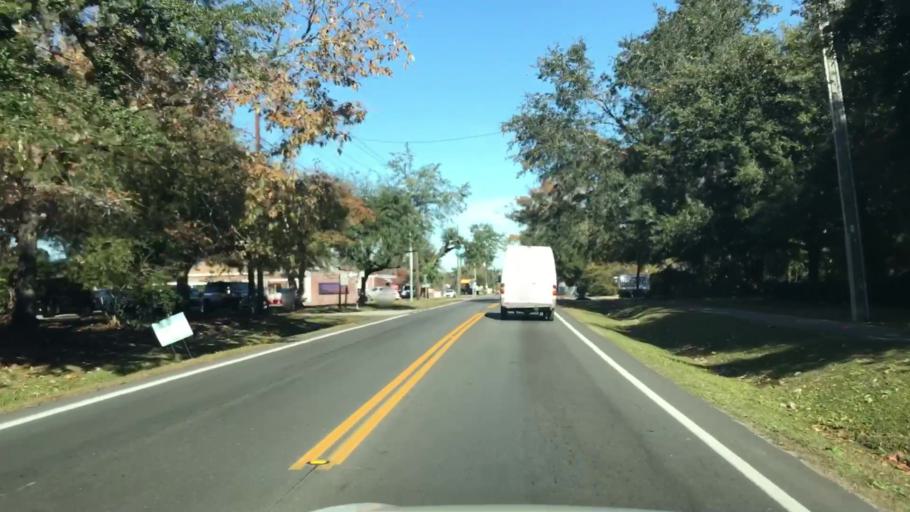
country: US
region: South Carolina
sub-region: Dorchester County
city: Summerville
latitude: 33.0075
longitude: -80.2361
